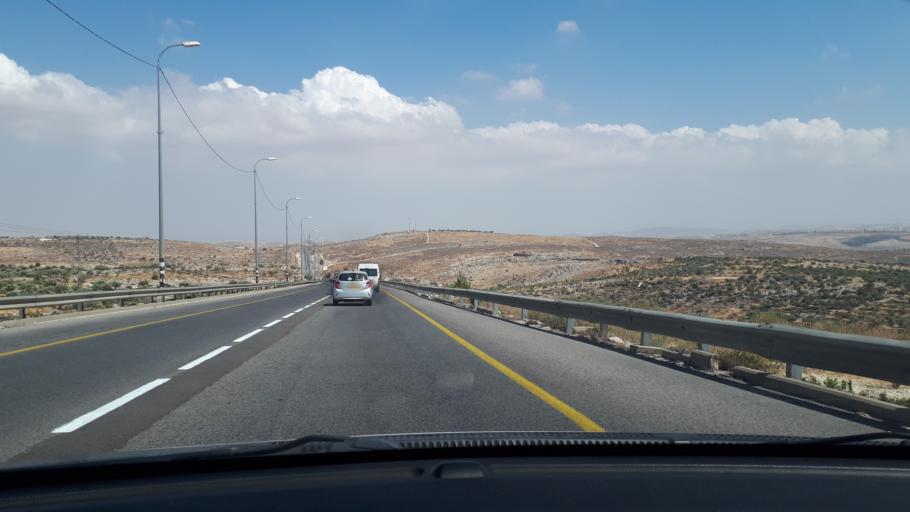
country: PS
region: West Bank
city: Burqah
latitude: 31.9033
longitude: 35.2583
